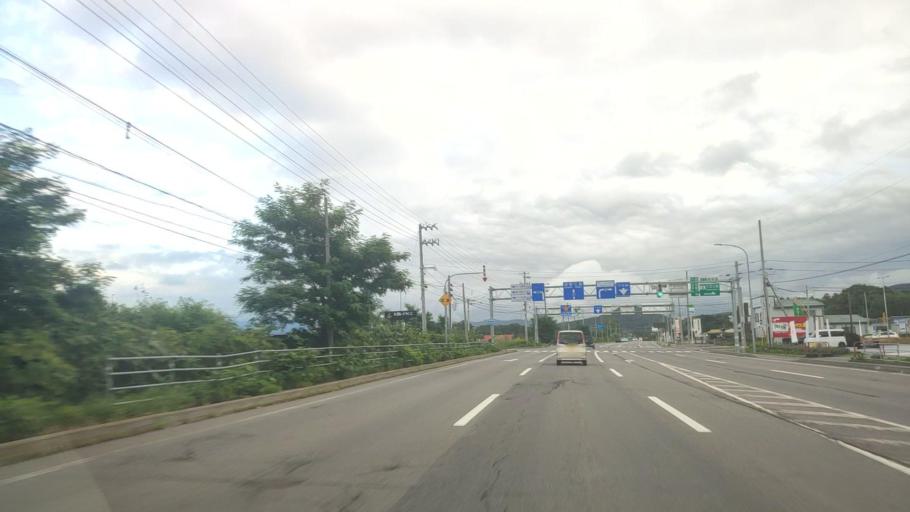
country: JP
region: Hokkaido
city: Nanae
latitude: 42.0081
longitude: 140.6312
